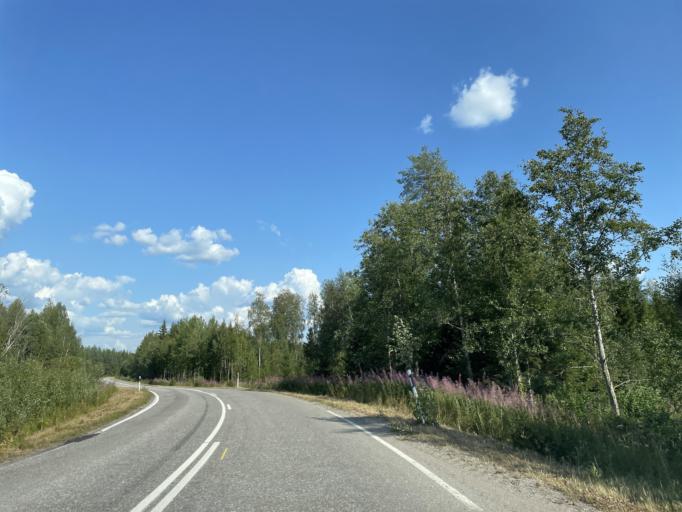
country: FI
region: Central Finland
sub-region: Saarijaervi-Viitasaari
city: Pihtipudas
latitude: 63.3651
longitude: 25.6995
